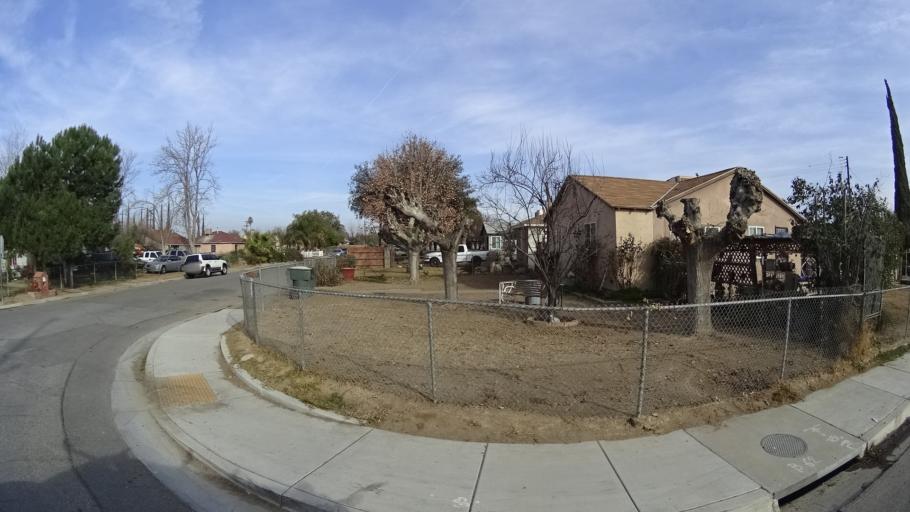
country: US
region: California
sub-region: Kern County
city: Bakersfield
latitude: 35.3614
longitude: -118.9573
